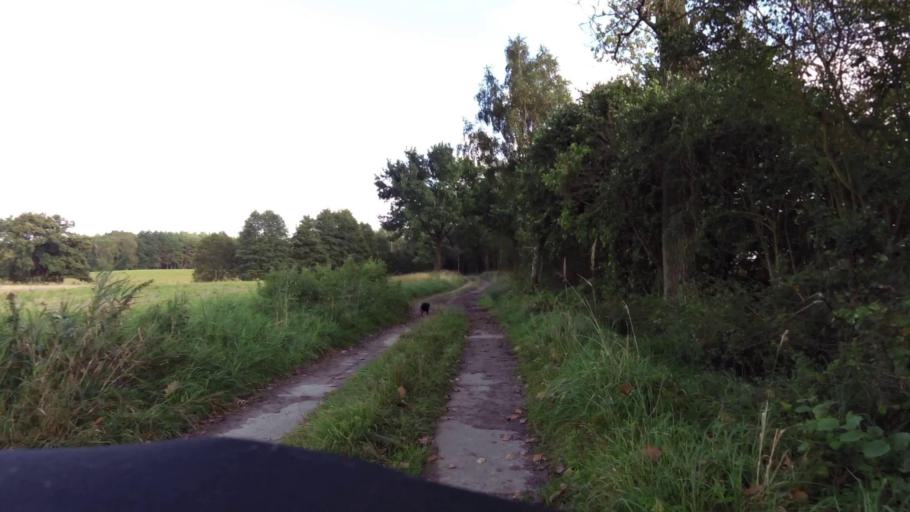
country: PL
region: West Pomeranian Voivodeship
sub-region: Powiat stargardzki
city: Marianowo
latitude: 53.3842
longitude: 15.3172
